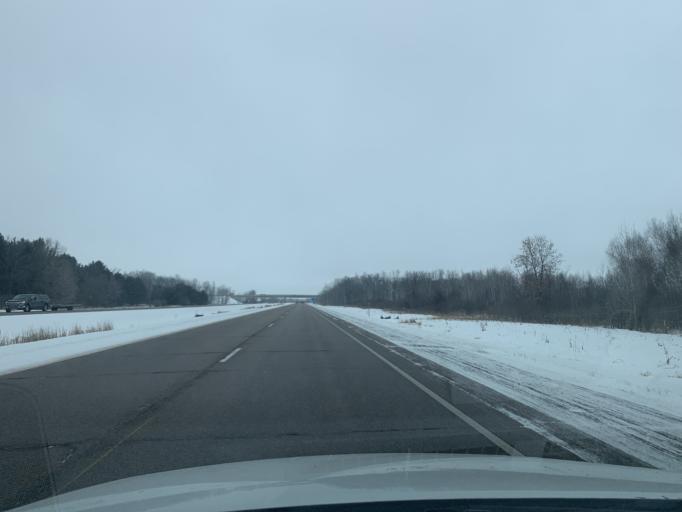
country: US
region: Minnesota
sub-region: Chisago County
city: Rush City
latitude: 45.6667
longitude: -92.9922
